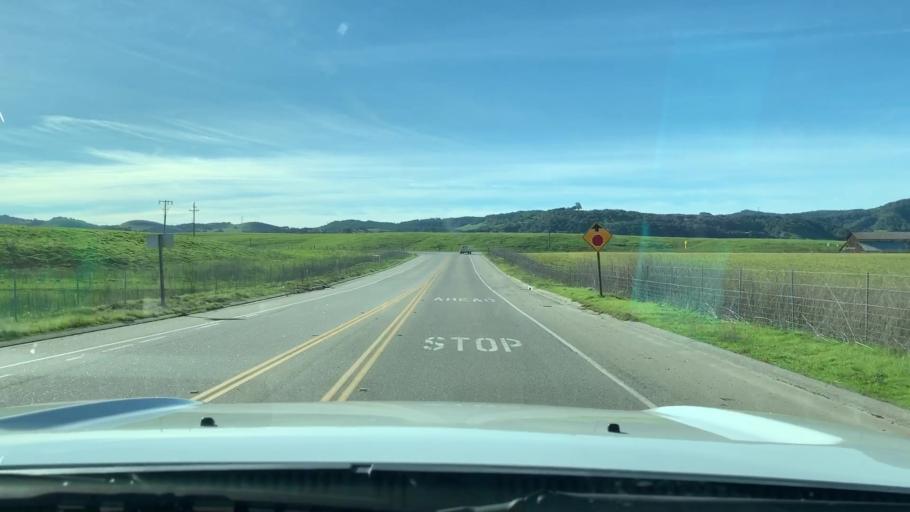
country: US
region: California
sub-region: San Luis Obispo County
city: San Luis Obispo
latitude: 35.2371
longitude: -120.6496
